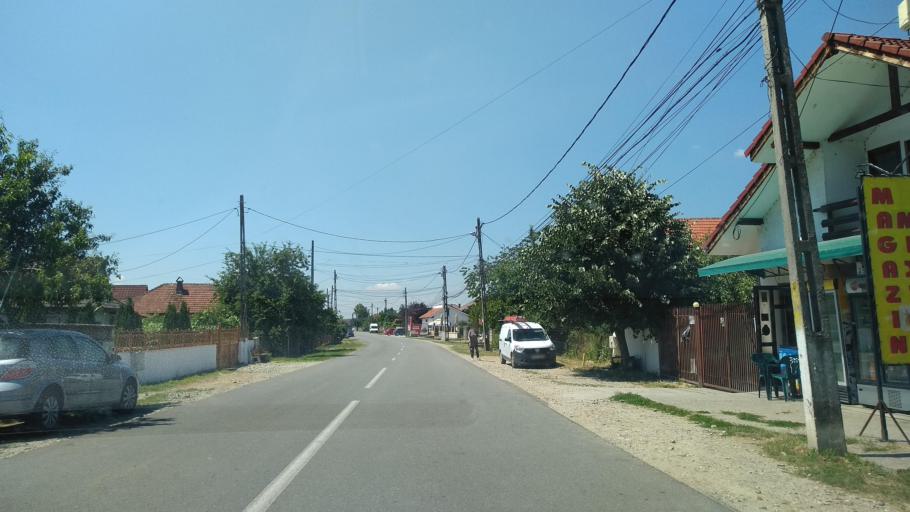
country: RO
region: Gorj
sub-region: Comuna Turcinesti
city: Turcinesti
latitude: 45.1083
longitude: 23.3167
